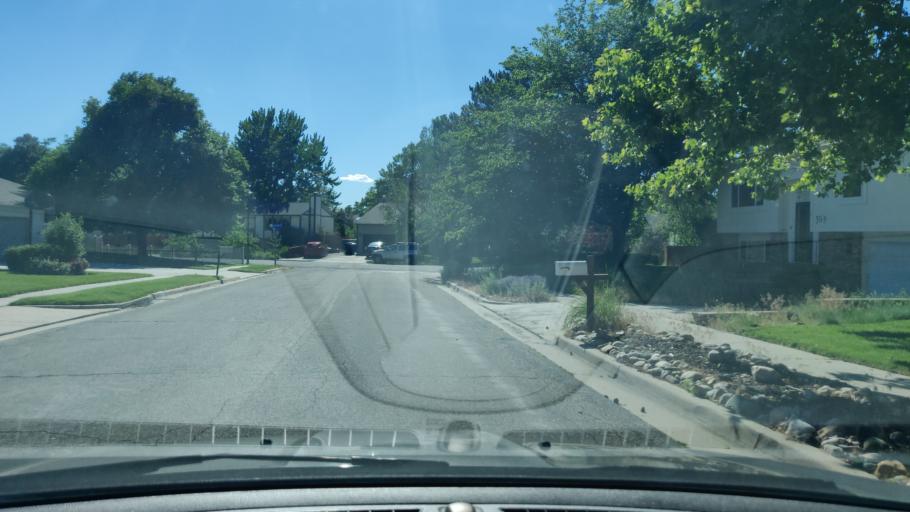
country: US
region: Utah
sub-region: Salt Lake County
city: Cottonwood Heights
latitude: 40.6220
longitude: -111.8036
